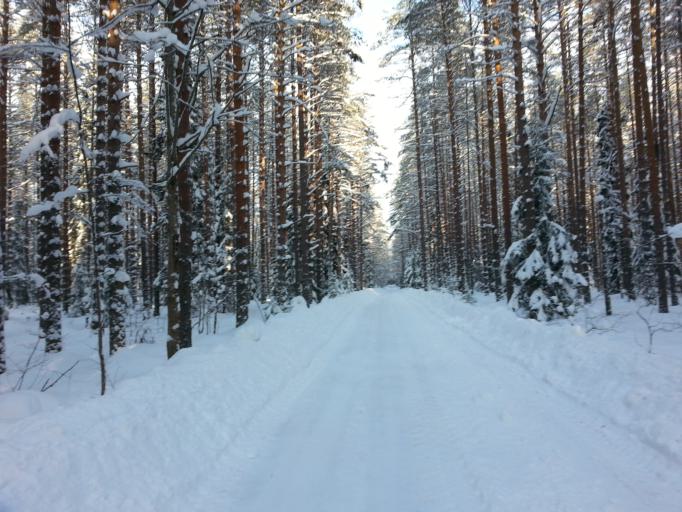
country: RU
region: Leningrad
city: Roshchino
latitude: 60.2140
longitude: 29.6061
